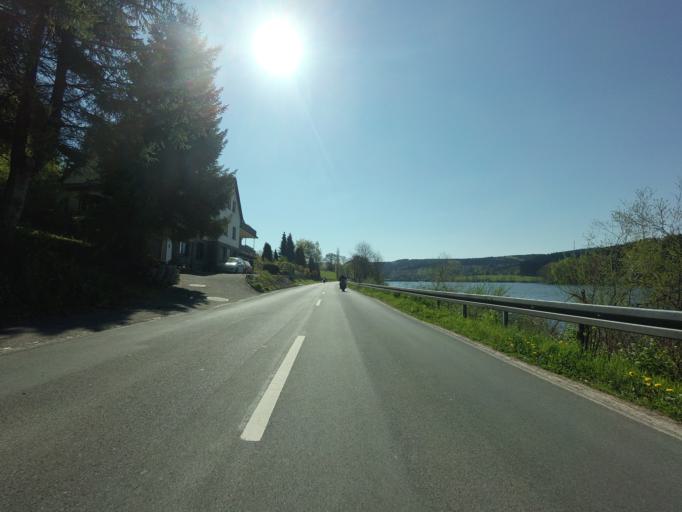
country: DE
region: North Rhine-Westphalia
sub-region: Regierungsbezirk Arnsberg
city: Drolshagen
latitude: 51.0788
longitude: 7.8003
